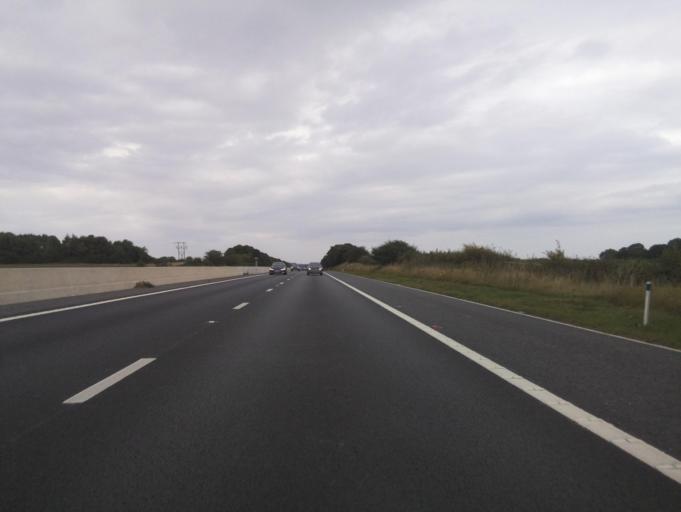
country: GB
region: England
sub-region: County Durham
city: Newton Aycliffe
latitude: 54.6140
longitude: -1.5324
